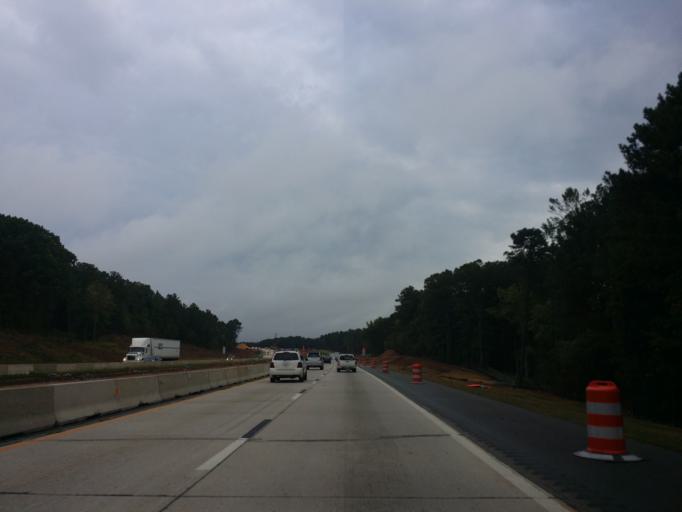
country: US
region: North Carolina
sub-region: Durham County
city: Durham
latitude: 35.9597
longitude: -78.8643
